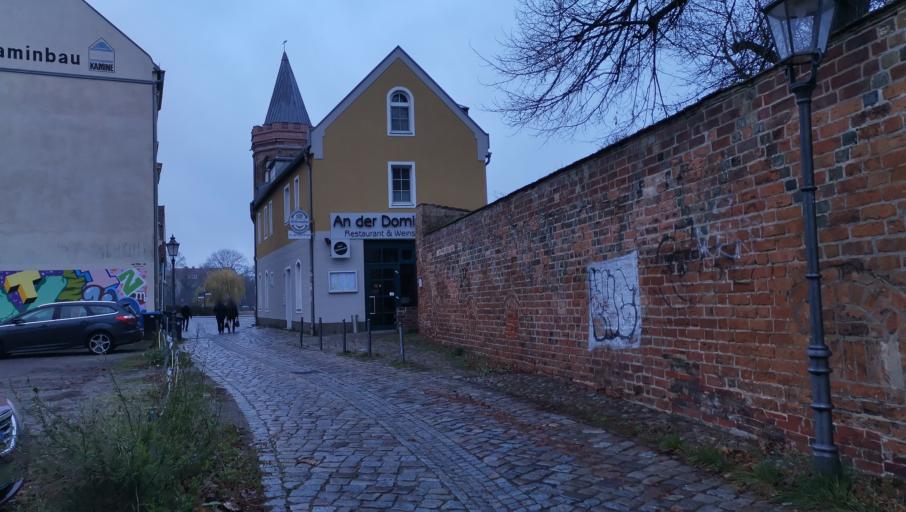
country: DE
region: Brandenburg
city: Brandenburg an der Havel
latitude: 52.4106
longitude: 12.5660
